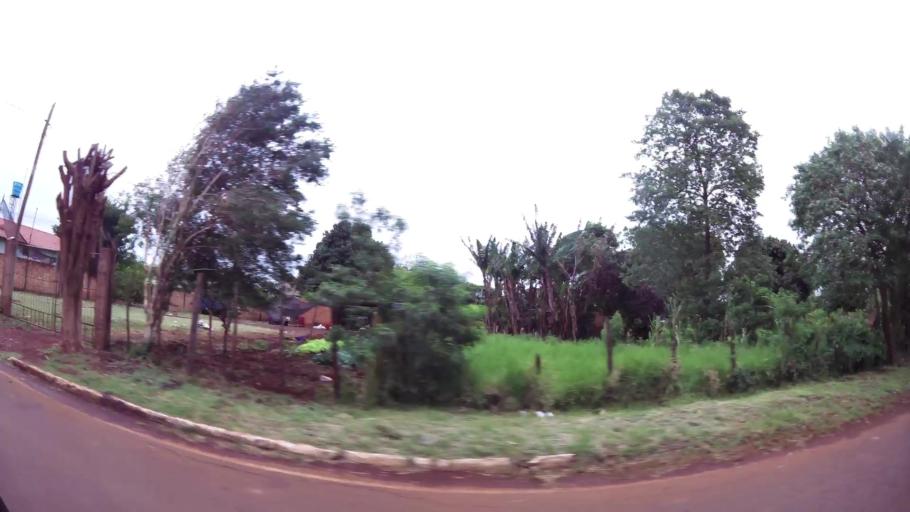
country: PY
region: Alto Parana
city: Presidente Franco
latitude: -25.4871
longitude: -54.7677
